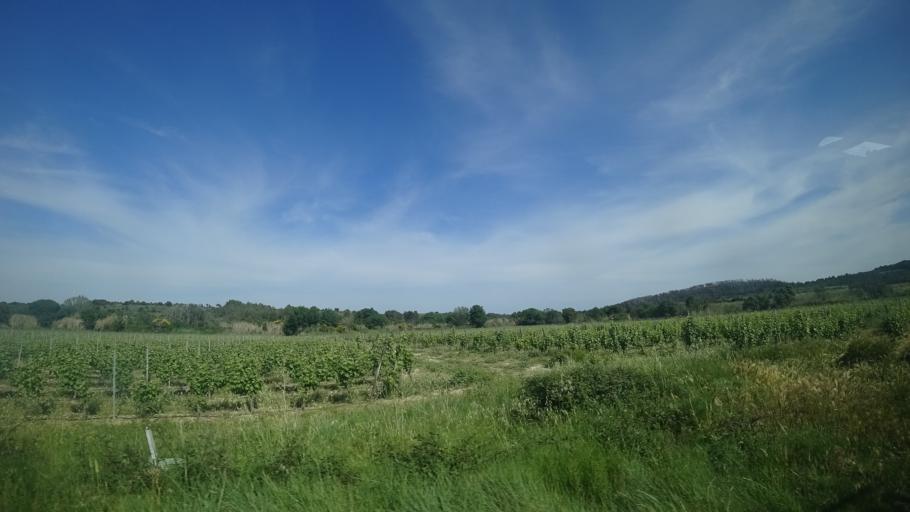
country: FR
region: Languedoc-Roussillon
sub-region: Departement de l'Aude
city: Ginestas
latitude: 43.2746
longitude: 2.8151
